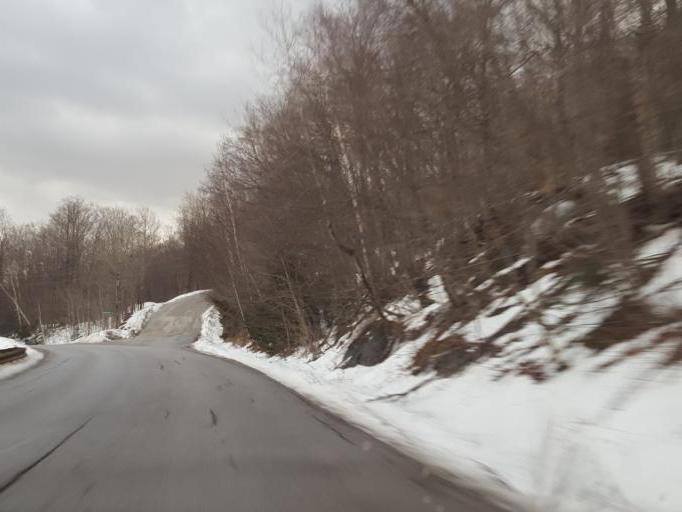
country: US
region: Vermont
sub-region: Rutland County
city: Rutland
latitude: 43.6207
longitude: -72.7710
